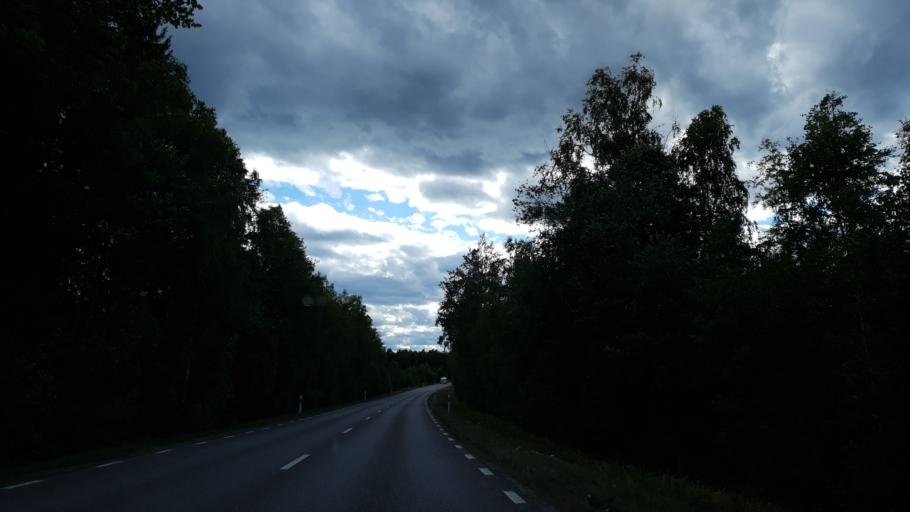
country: SE
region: Kalmar
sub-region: Emmaboda Kommun
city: Emmaboda
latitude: 56.6231
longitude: 15.5901
